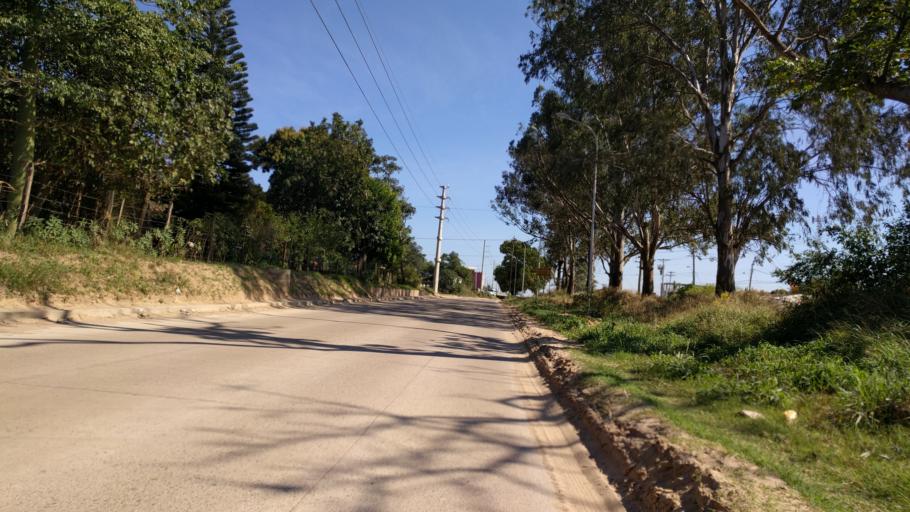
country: BO
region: Santa Cruz
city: Santa Cruz de la Sierra
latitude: -17.8670
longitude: -63.2008
